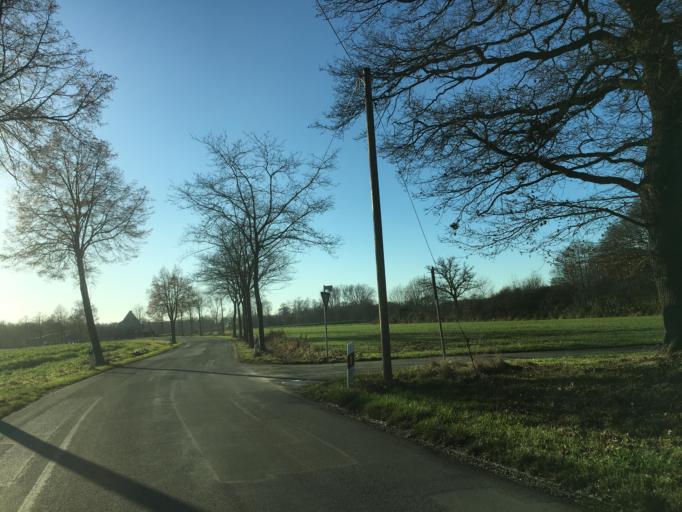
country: DE
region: North Rhine-Westphalia
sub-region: Regierungsbezirk Munster
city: Dulmen
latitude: 51.8568
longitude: 7.2934
